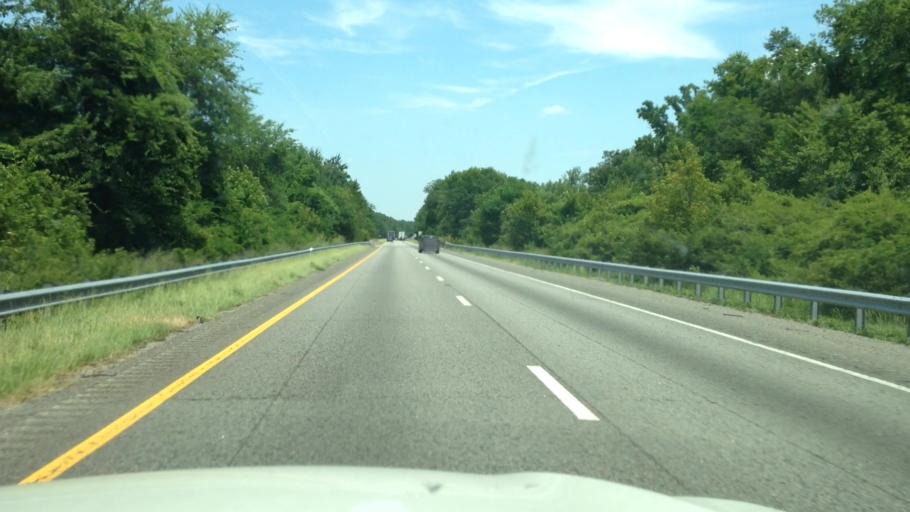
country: US
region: South Carolina
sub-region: Florence County
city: Florence
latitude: 34.3043
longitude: -79.6249
